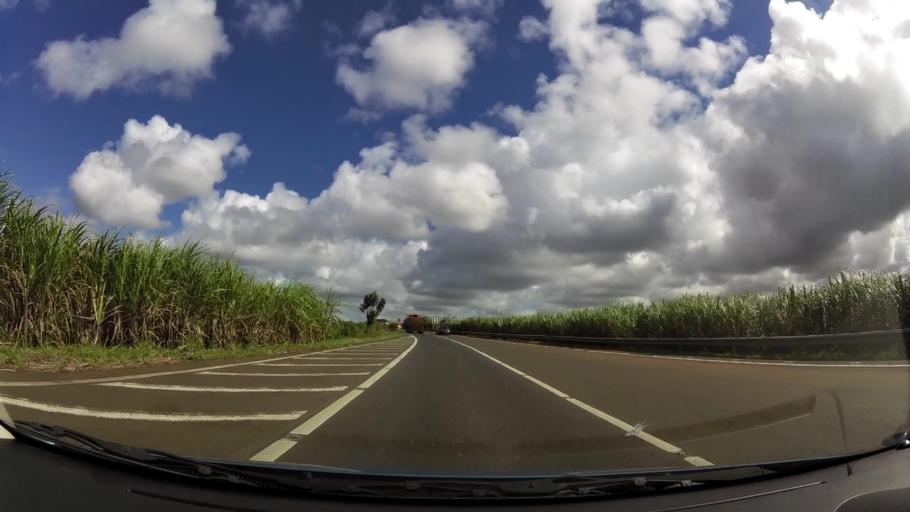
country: MU
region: Grand Port
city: Plaine Magnien
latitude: -20.4203
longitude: 57.6653
